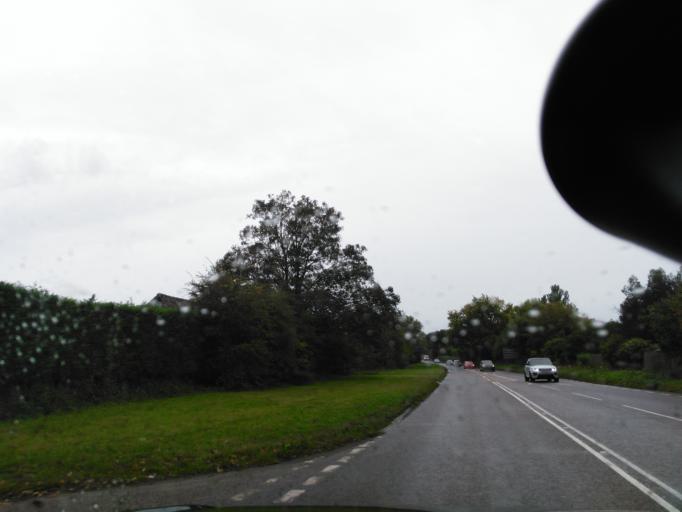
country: GB
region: England
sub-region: Wiltshire
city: Lacock
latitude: 51.4281
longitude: -2.1292
